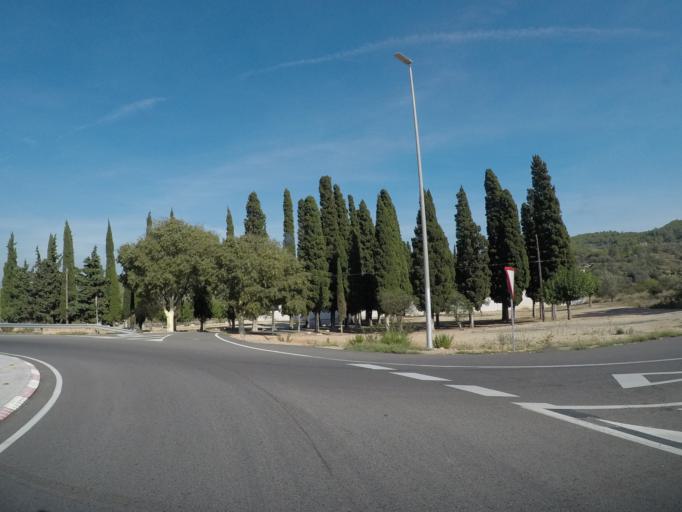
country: ES
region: Catalonia
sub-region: Provincia de Tarragona
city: El Perello
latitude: 40.8816
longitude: 0.7183
